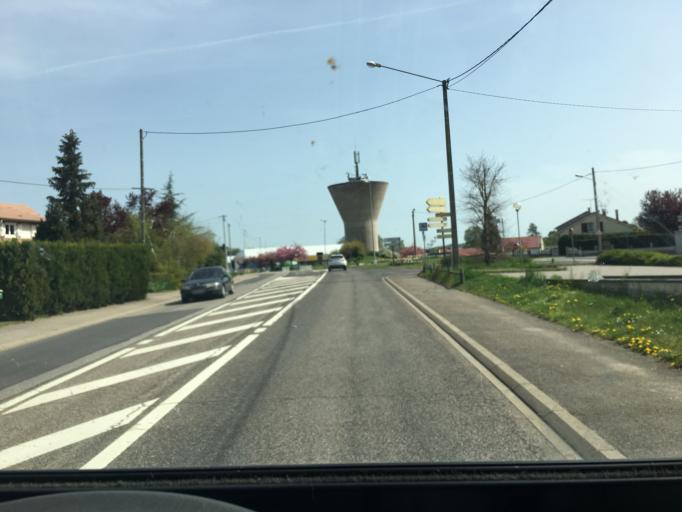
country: FR
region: Lorraine
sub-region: Departement de Meurthe-et-Moselle
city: Saint-Nicolas-de-Port
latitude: 48.6244
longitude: 6.2921
